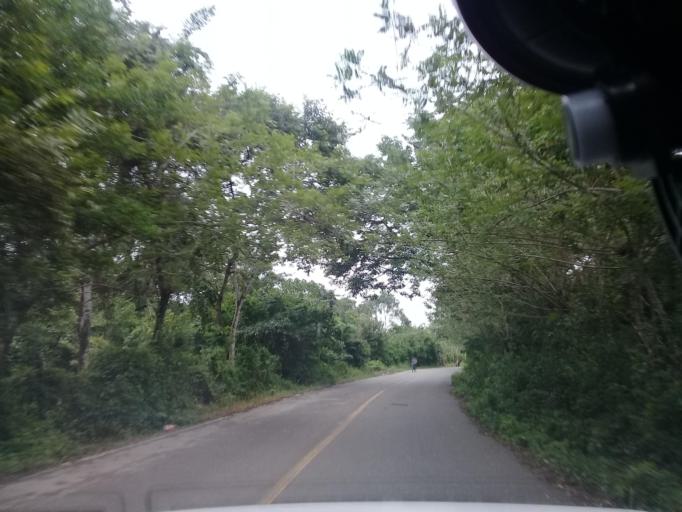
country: MX
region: Veracruz
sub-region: Chalma
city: San Pedro Coyutla
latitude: 21.2086
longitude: -98.4042
